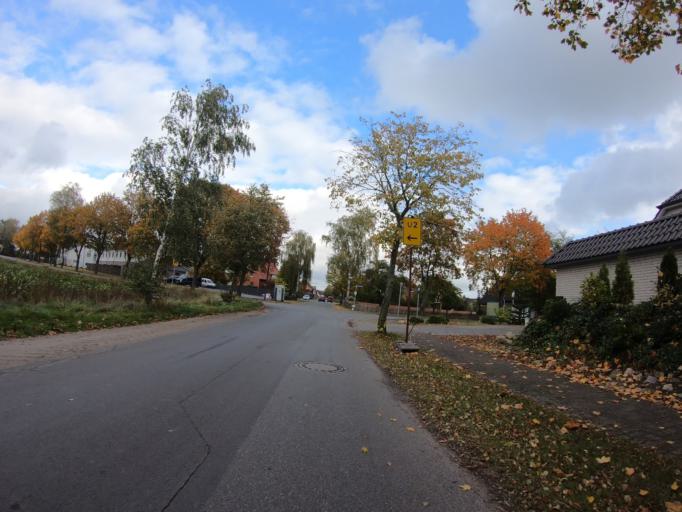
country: DE
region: Lower Saxony
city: Wahrenholz
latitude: 52.6076
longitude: 10.5946
